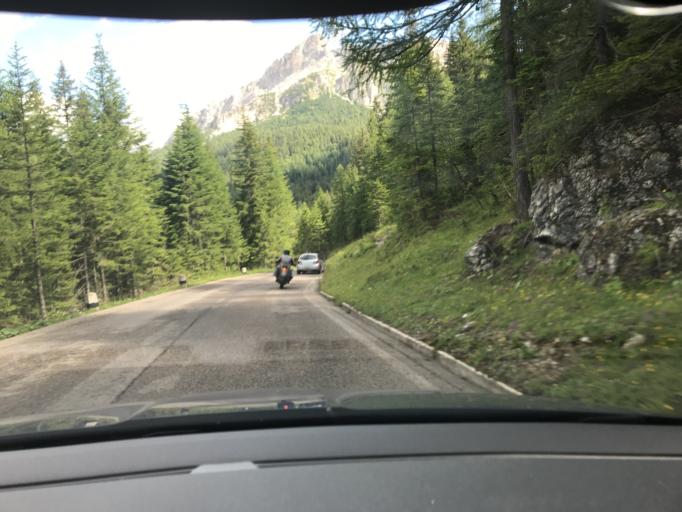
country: IT
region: Veneto
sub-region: Provincia di Belluno
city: Livinallongo del Col di Lana
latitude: 46.4996
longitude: 11.9916
